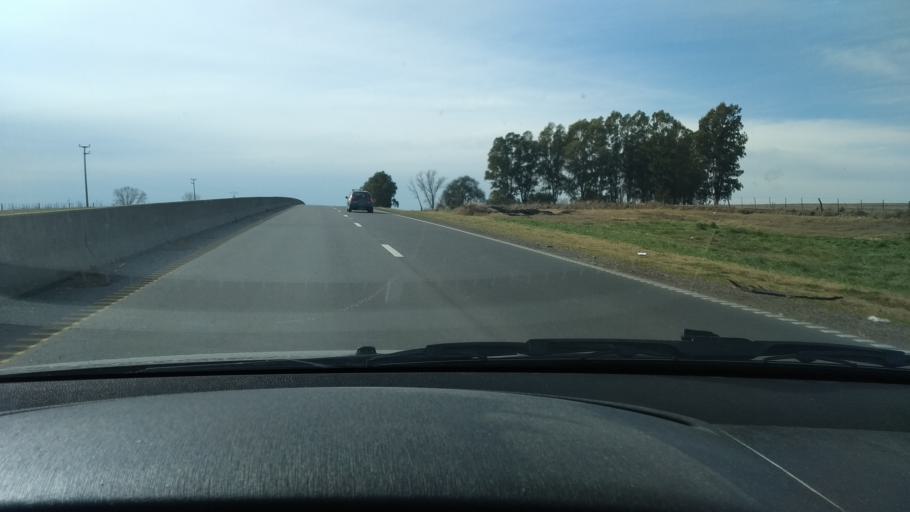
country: AR
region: Buenos Aires
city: Olavarria
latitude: -36.8932
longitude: -60.1629
